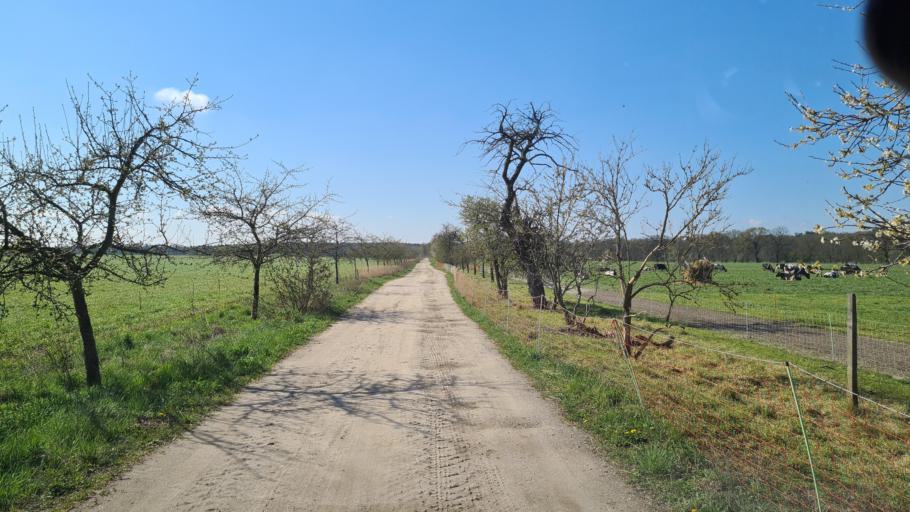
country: DE
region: Brandenburg
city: Altdobern
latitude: 51.7093
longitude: 14.0456
